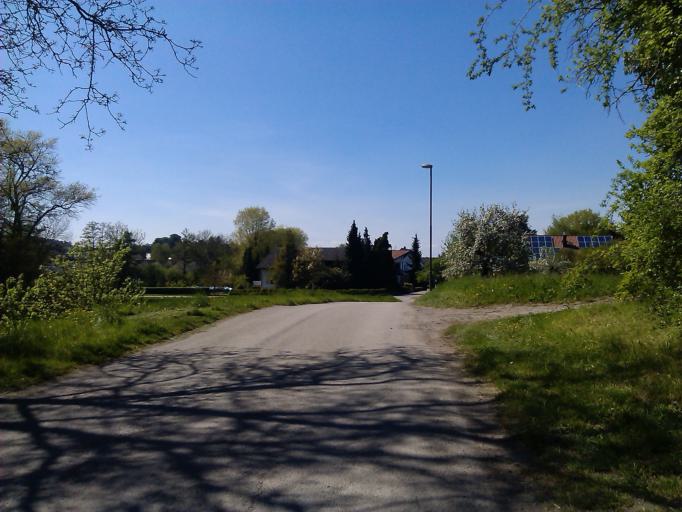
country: DE
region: Baden-Wuerttemberg
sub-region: Karlsruhe Region
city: Sulzfeld
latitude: 49.0971
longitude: 8.8677
